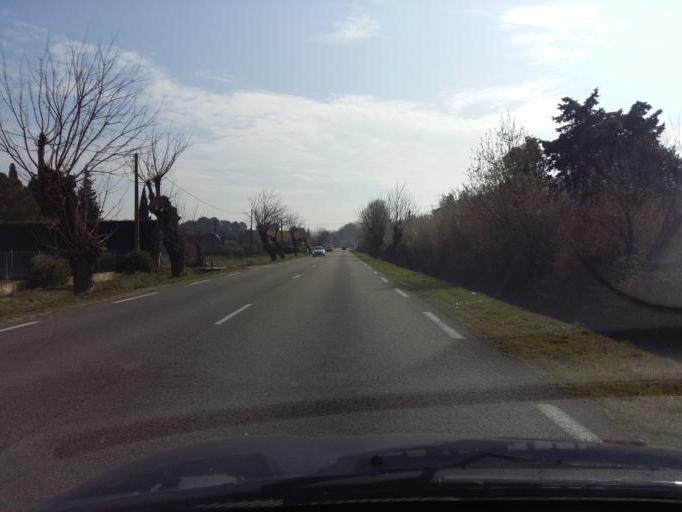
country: FR
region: Provence-Alpes-Cote d'Azur
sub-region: Departement des Bouches-du-Rhone
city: Orgon
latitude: 43.8034
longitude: 5.0017
